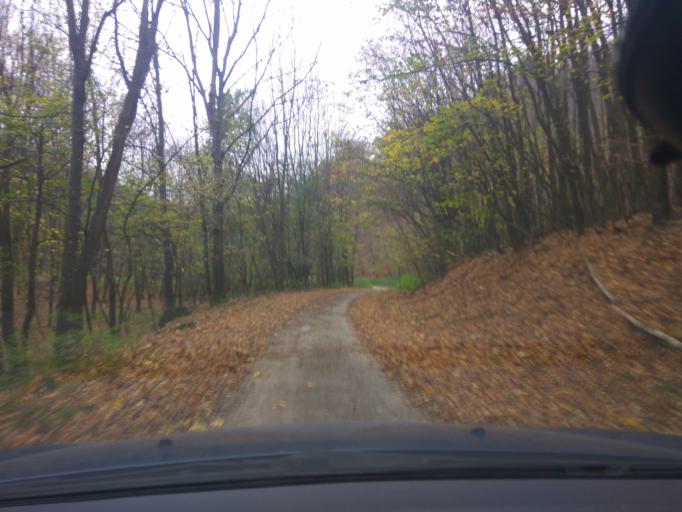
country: SK
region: Trnavsky
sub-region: Okres Trnava
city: Piestany
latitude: 48.6006
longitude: 17.9545
